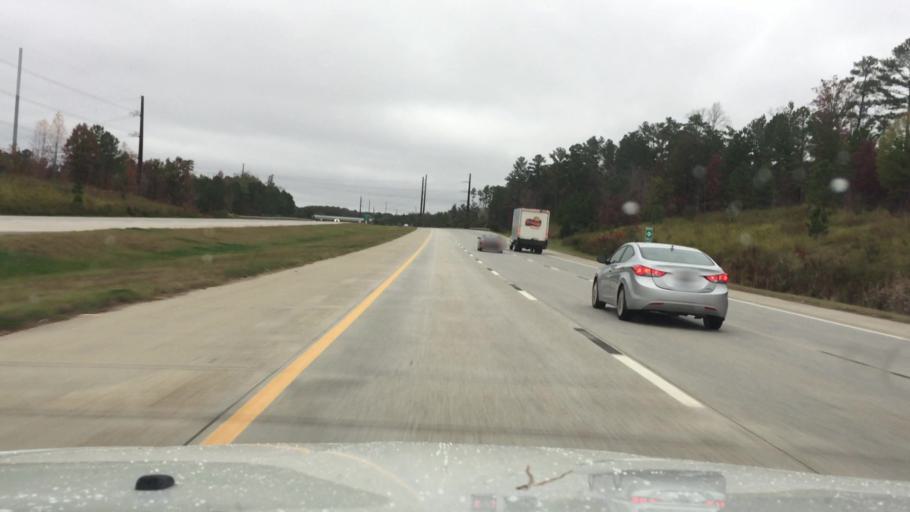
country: US
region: North Carolina
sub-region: Wake County
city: Green Level
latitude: 35.8159
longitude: -78.8921
